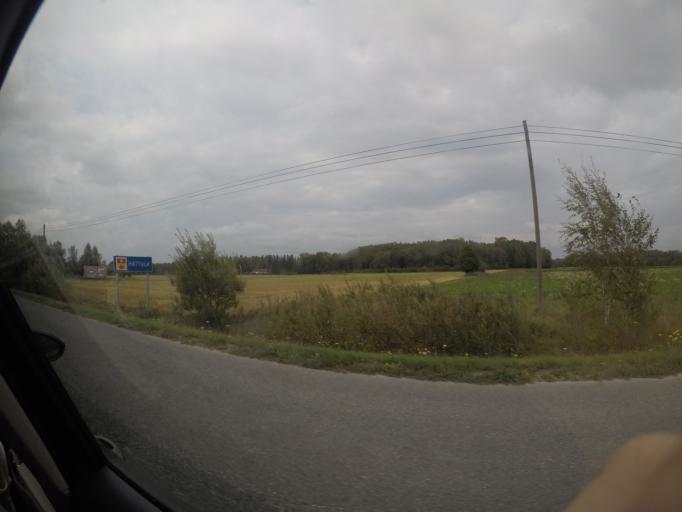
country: FI
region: Haeme
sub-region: Haemeenlinna
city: Parola
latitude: 61.0331
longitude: 24.4141
